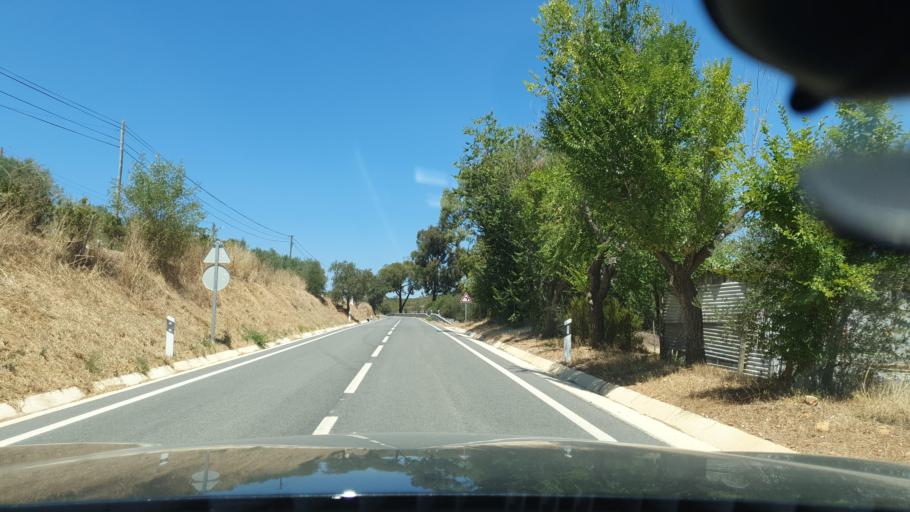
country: PT
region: Beja
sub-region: Odemira
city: Odemira
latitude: 37.5140
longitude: -8.4768
